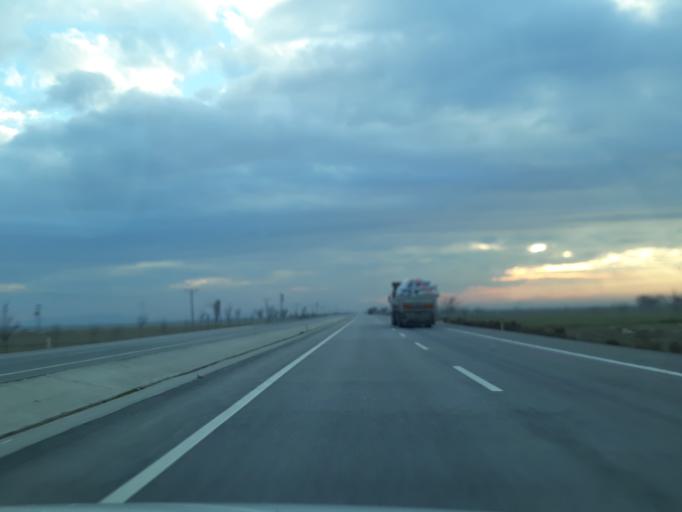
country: TR
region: Konya
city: Hotamis
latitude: 37.7109
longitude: 33.2911
